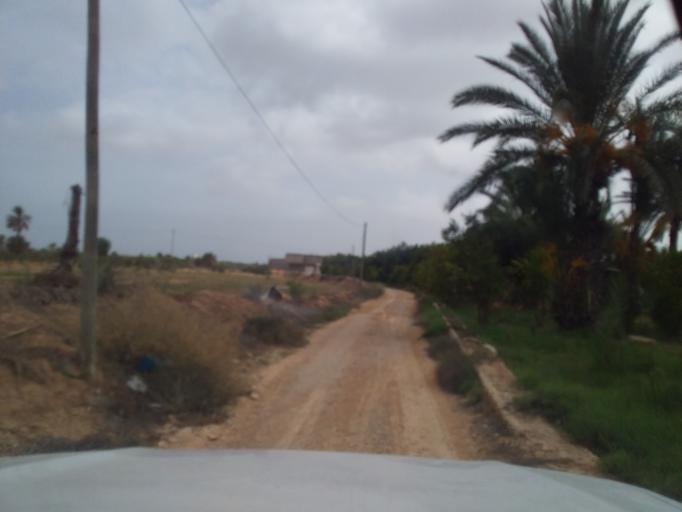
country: TN
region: Qabis
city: Gabes
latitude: 33.6284
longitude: 10.3080
